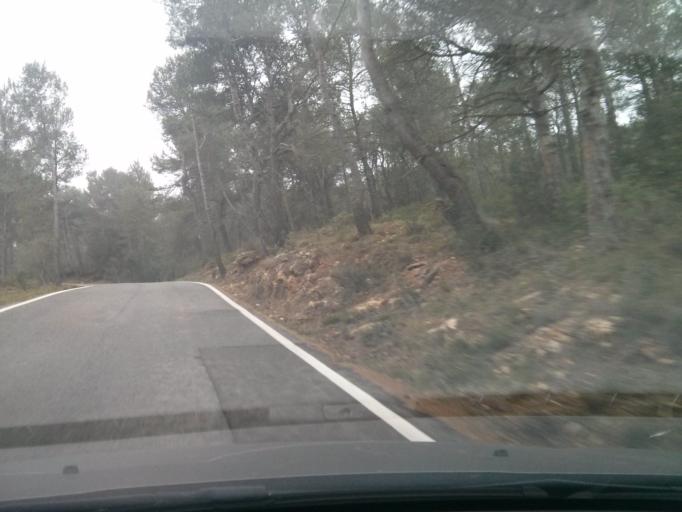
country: ES
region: Catalonia
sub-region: Provincia de Tarragona
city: Sant Jaume dels Domenys
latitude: 41.3413
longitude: 1.5222
